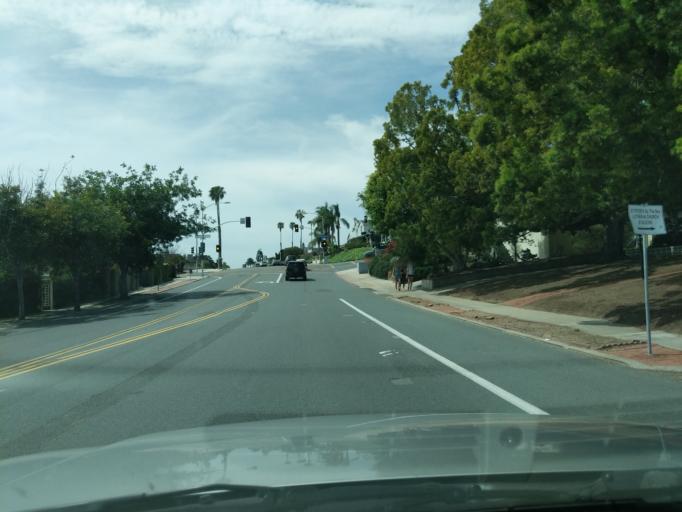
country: US
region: California
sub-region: San Diego County
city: Coronado
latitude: 32.7303
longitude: -117.2434
